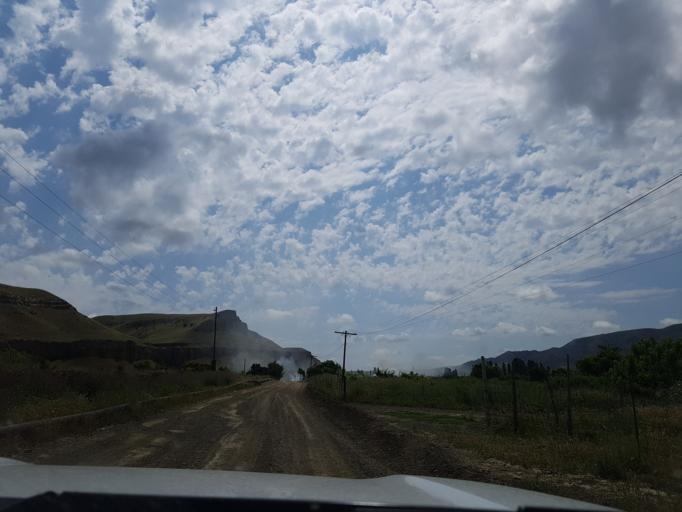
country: TM
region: Ahal
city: Baharly
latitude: 38.2266
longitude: 56.8753
